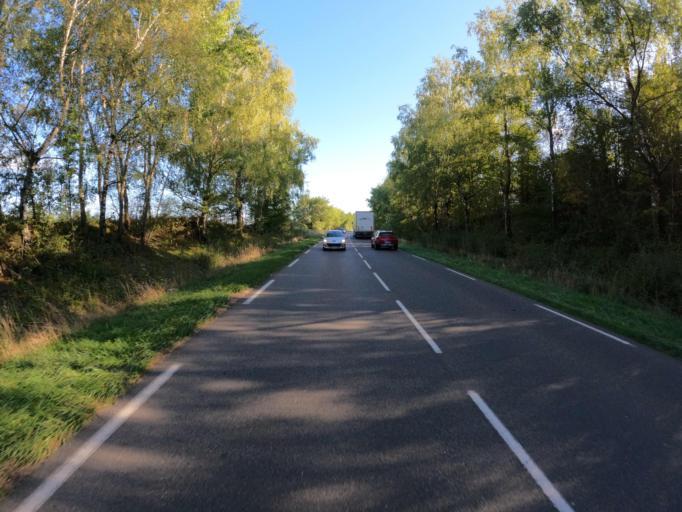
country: FR
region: Bourgogne
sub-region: Departement de Saone-et-Loire
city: Montchanin
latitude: 46.7424
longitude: 4.4450
